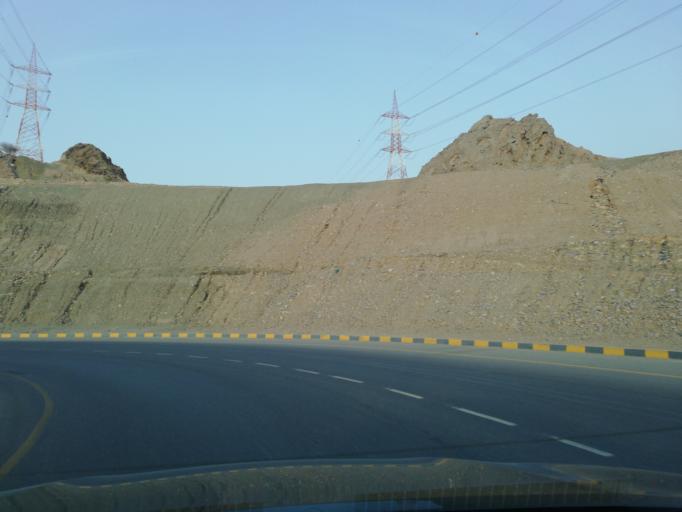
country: OM
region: Muhafazat Masqat
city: Bawshar
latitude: 23.5784
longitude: 58.4460
